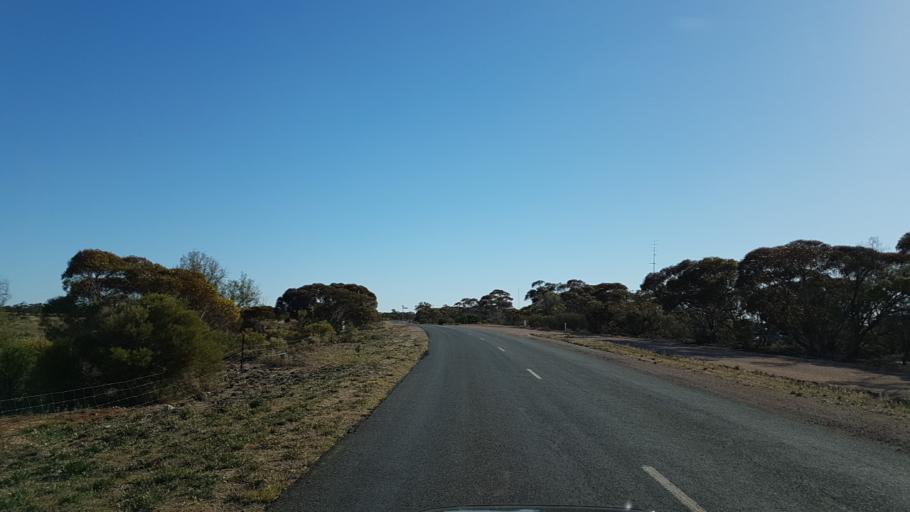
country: AU
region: South Australia
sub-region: Loxton Waikerie
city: Waikerie
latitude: -34.1832
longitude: 140.0221
